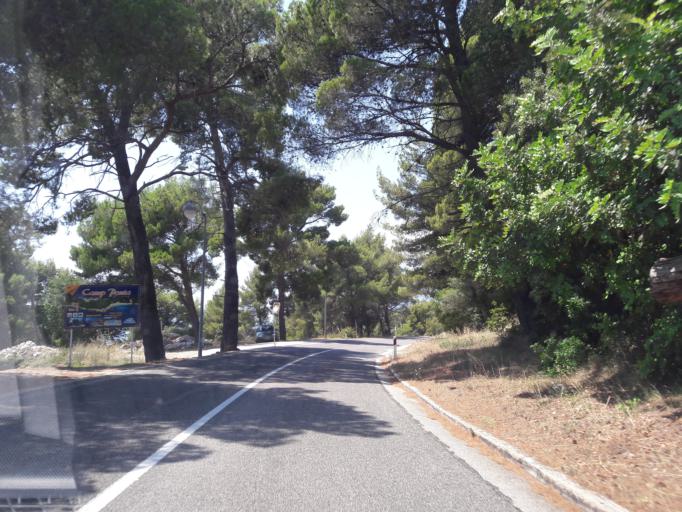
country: HR
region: Dubrovacko-Neretvanska
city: Orebic
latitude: 42.9791
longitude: 17.2236
